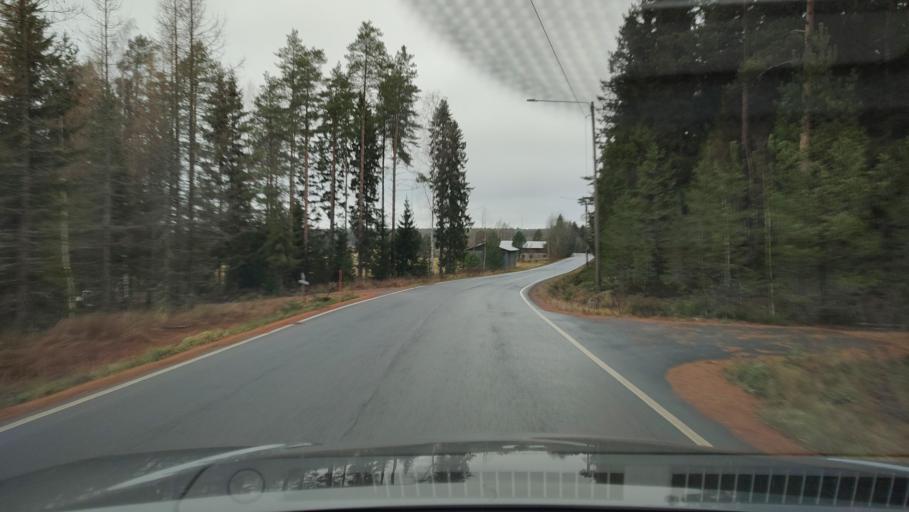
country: FI
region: Southern Ostrobothnia
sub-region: Suupohja
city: Karijoki
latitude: 62.1397
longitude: 21.6850
